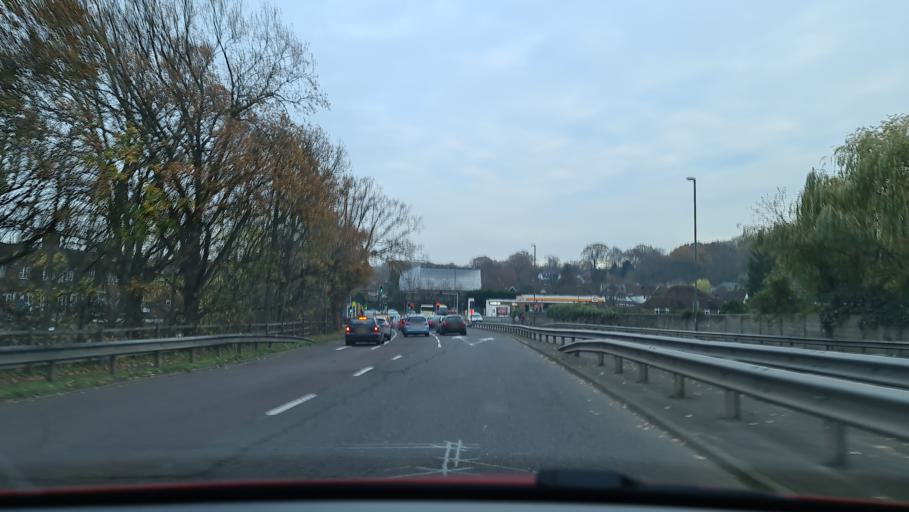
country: GB
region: England
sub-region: Surrey
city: Hinchley Wood
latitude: 51.3744
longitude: -0.3407
